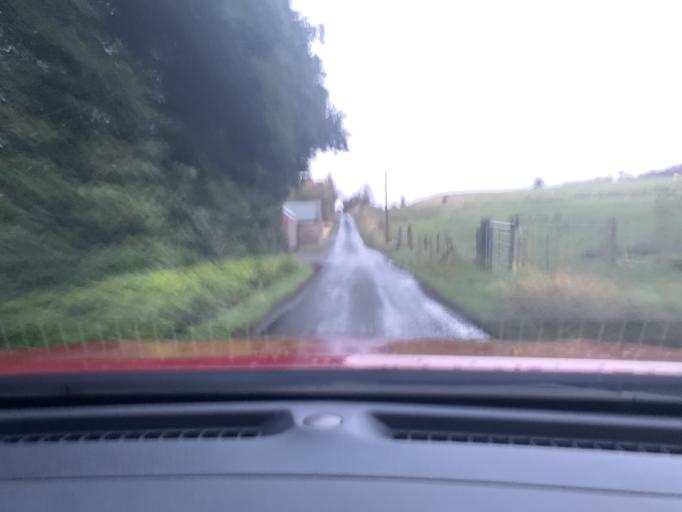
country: IE
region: Connaught
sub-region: Sligo
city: Ballymote
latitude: 54.0728
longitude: -8.3905
